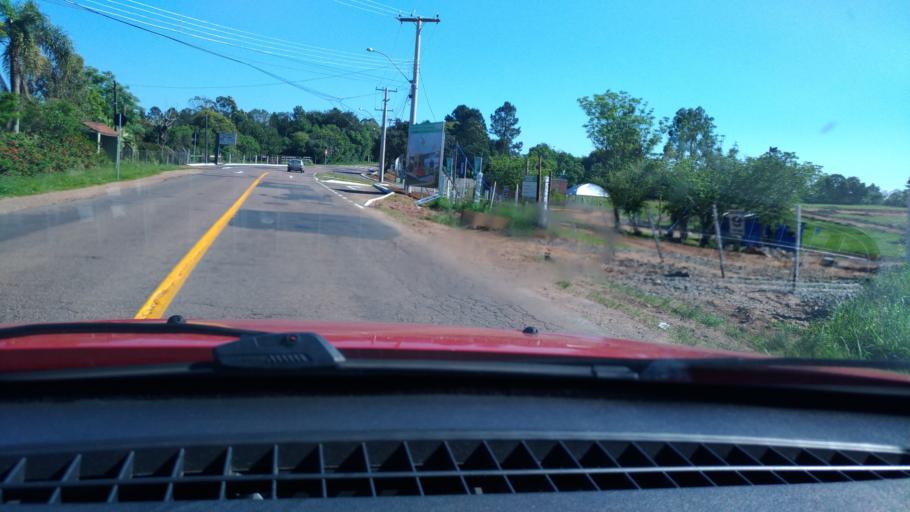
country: BR
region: Rio Grande do Sul
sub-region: Viamao
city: Viamao
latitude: -30.0554
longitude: -51.0603
